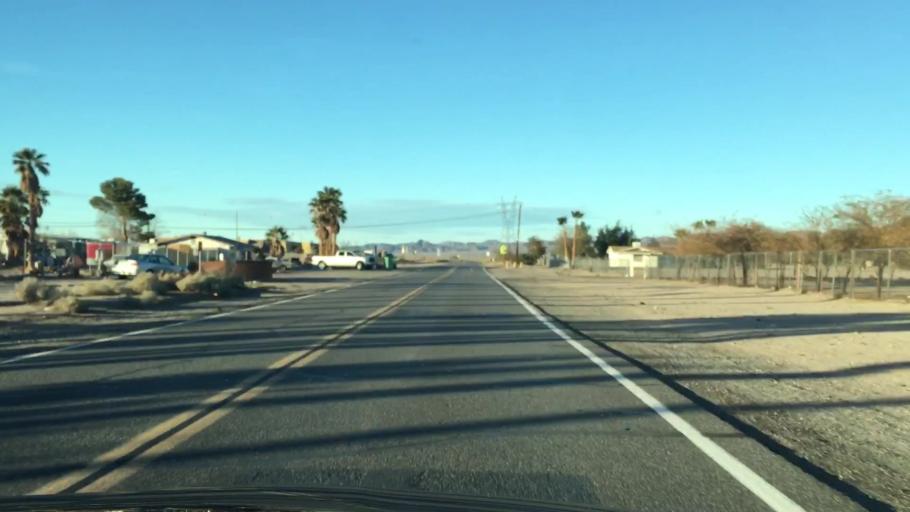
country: US
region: California
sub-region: San Bernardino County
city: Fort Irwin
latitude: 35.2736
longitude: -116.0750
